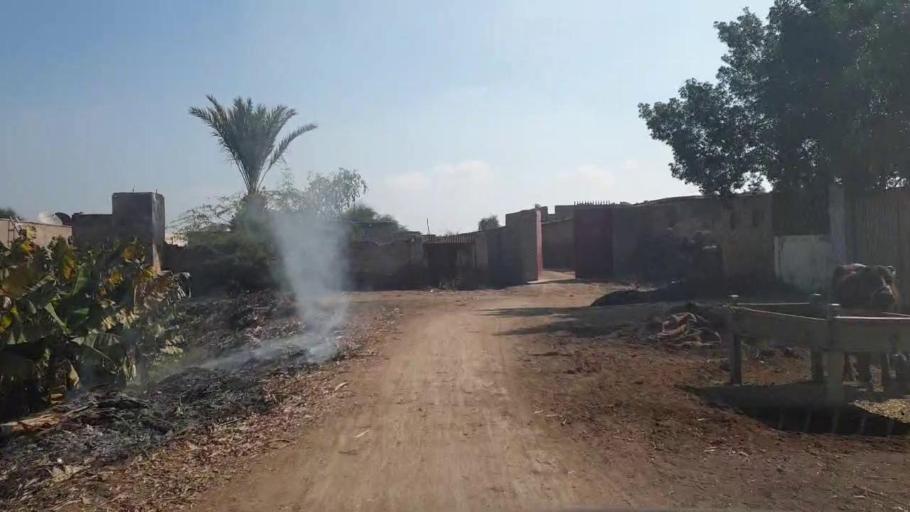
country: PK
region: Sindh
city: Shahdadpur
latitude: 25.9300
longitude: 68.5895
